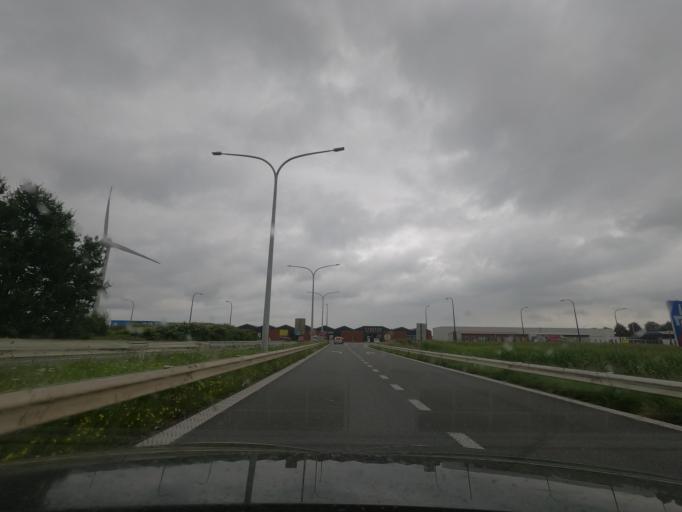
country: BE
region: Wallonia
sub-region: Province de Namur
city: Floreffe
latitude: 50.4942
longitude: 4.7222
